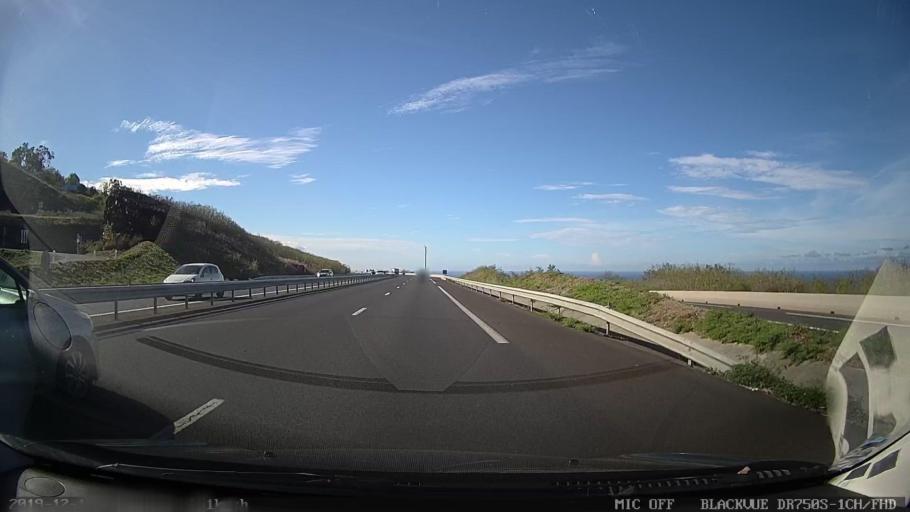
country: RE
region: Reunion
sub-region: Reunion
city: Saint-Leu
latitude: -21.1390
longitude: 55.2852
